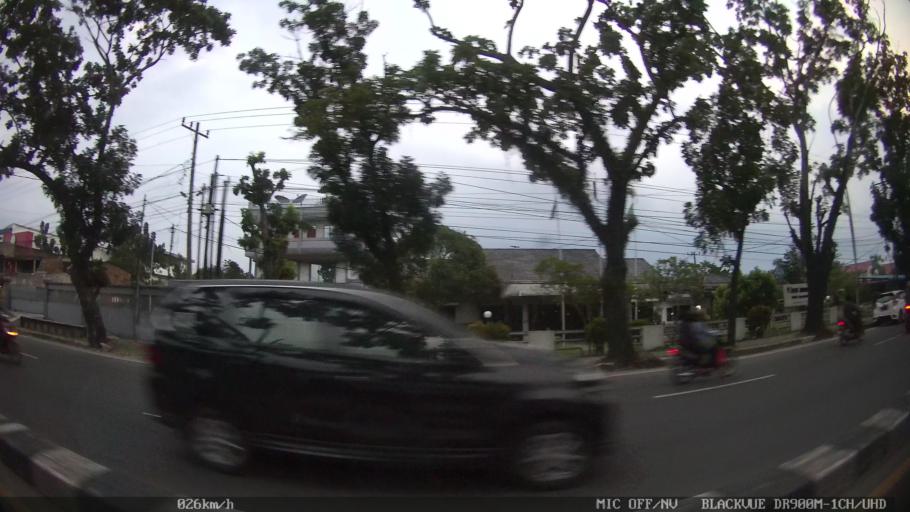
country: ID
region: North Sumatra
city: Sunggal
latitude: 3.5935
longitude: 98.6189
